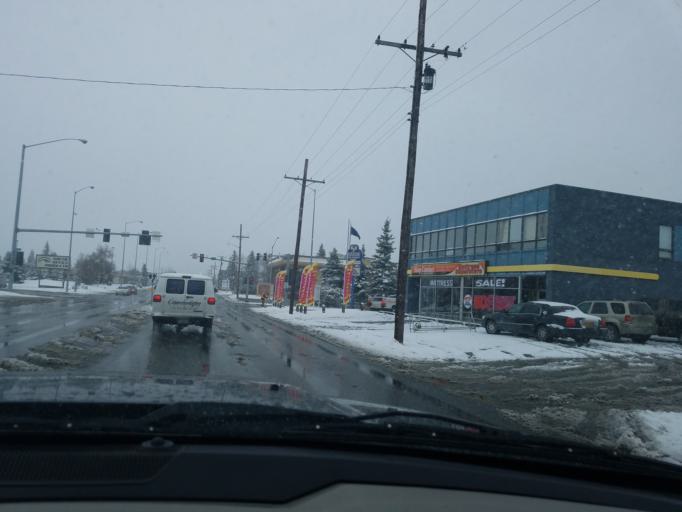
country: US
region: Alaska
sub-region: Anchorage Municipality
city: Anchorage
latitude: 61.1982
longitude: -149.8817
